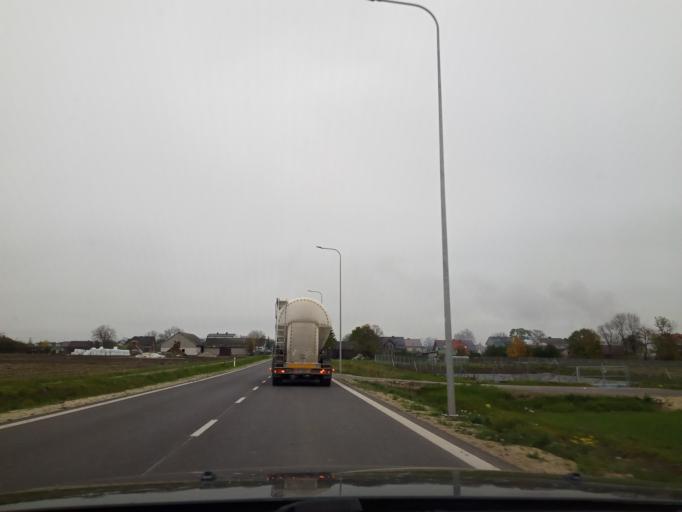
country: PL
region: Swietokrzyskie
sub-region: Powiat jedrzejowski
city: Jedrzejow
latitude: 50.5882
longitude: 20.3208
